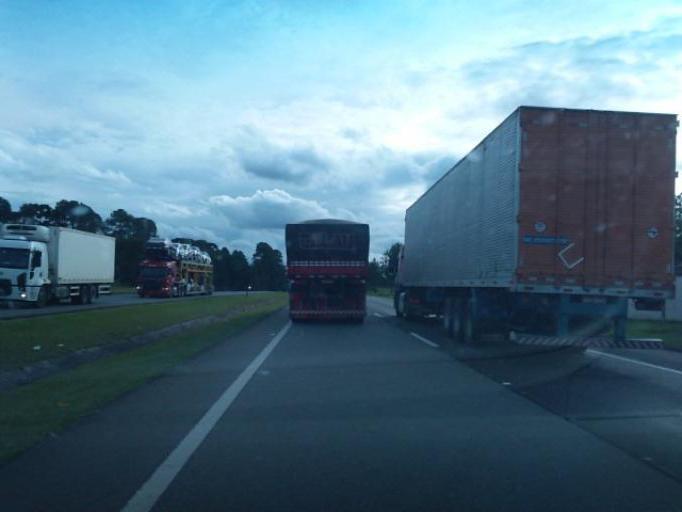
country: BR
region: Parana
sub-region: Piraquara
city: Piraquara
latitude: -25.4164
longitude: -49.0687
